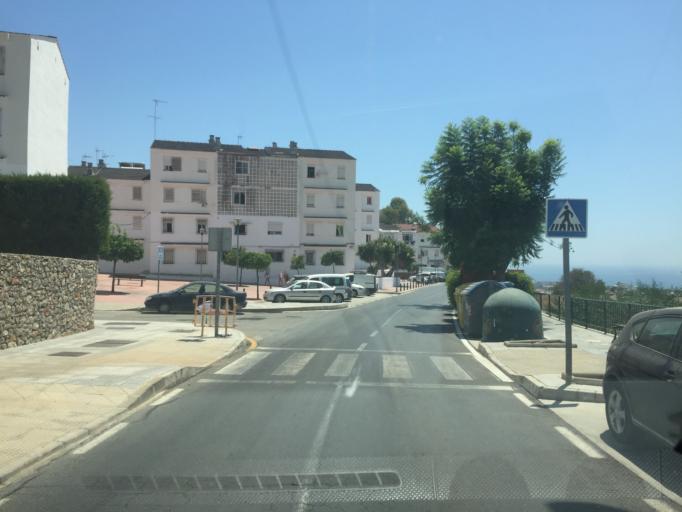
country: ES
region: Andalusia
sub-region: Provincia de Malaga
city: Nerja
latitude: 36.7641
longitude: -3.8715
